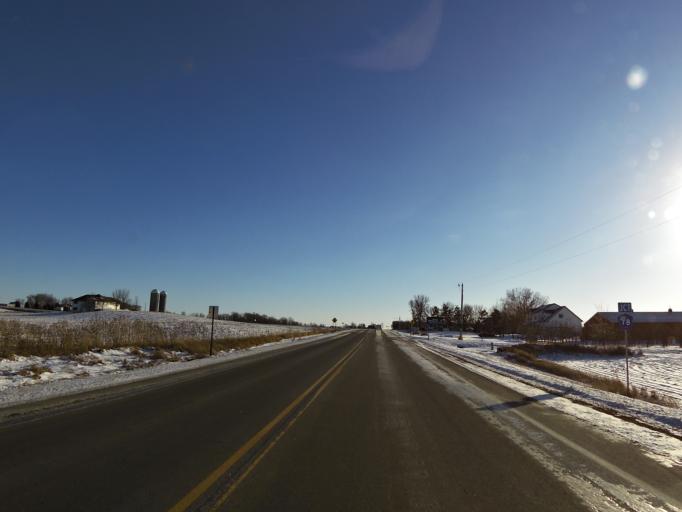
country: US
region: Minnesota
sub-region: Carver County
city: Chaska
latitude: 44.7642
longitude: -93.5612
